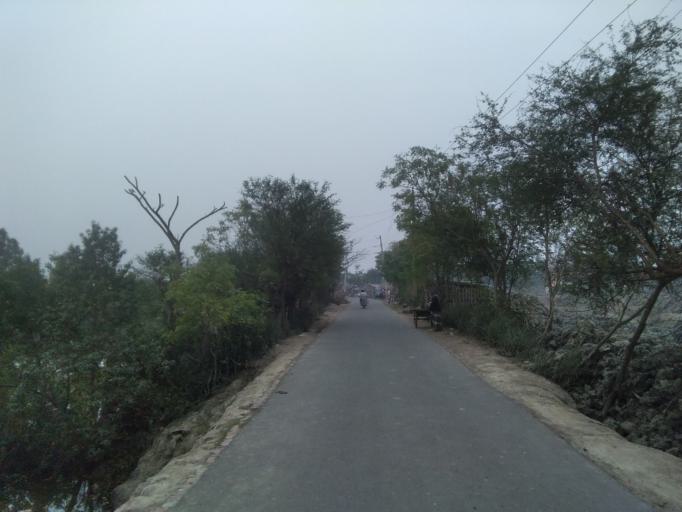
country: BD
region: Khulna
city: Satkhira
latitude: 22.5841
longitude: 89.0667
